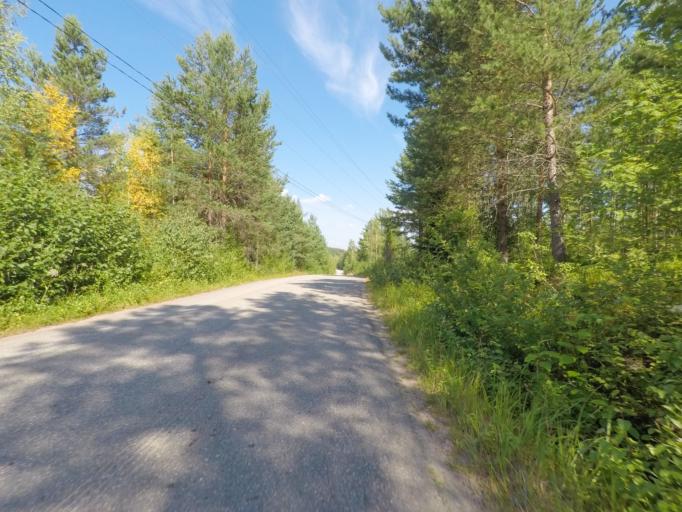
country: FI
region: Southern Savonia
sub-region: Mikkeli
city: Puumala
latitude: 61.4070
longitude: 28.0855
